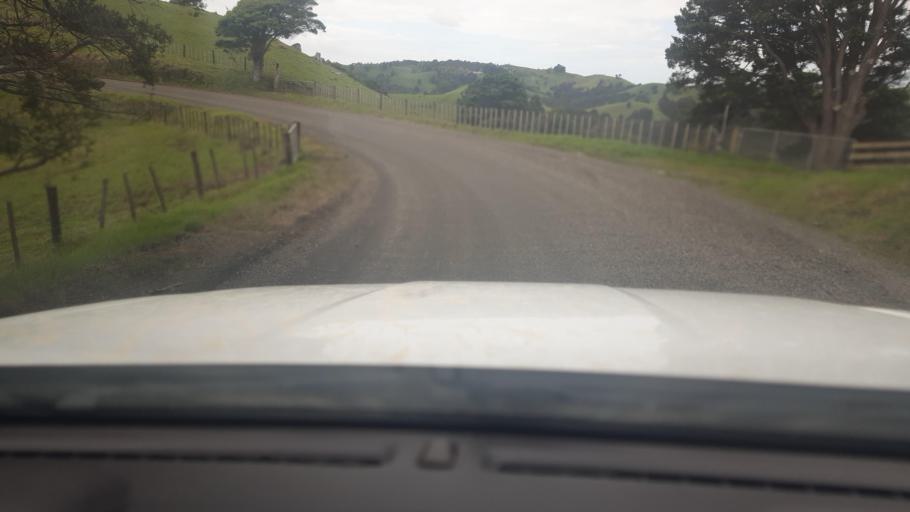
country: NZ
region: Northland
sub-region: Far North District
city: Kaitaia
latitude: -35.0818
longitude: 173.3226
